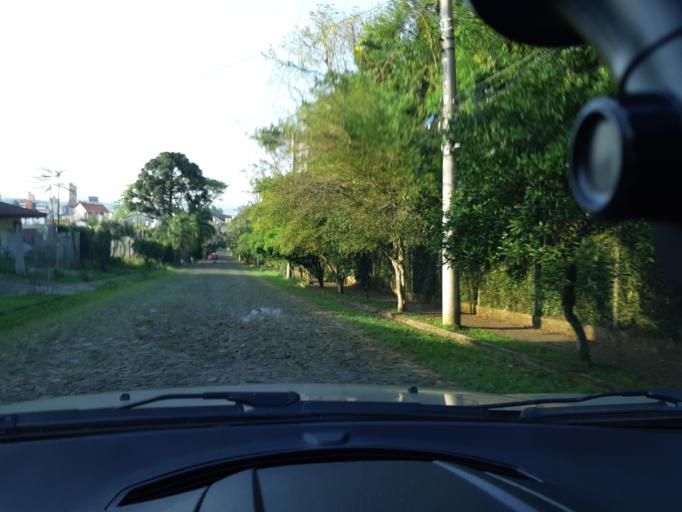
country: BR
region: Rio Grande do Sul
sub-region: Sao Leopoldo
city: Sao Leopoldo
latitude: -29.7757
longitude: -51.1402
